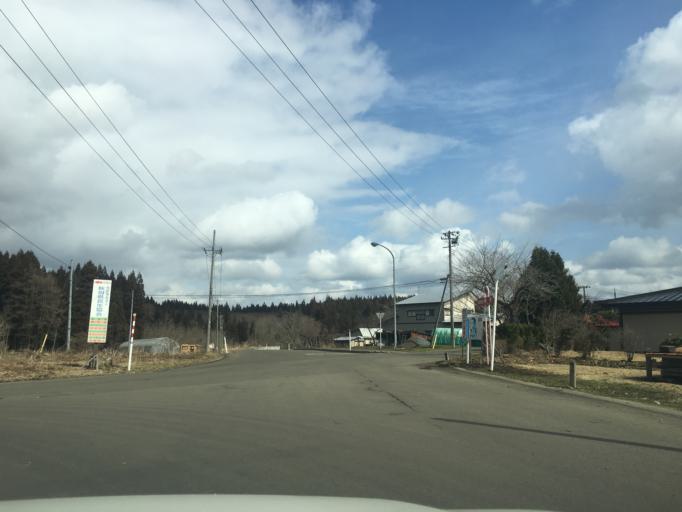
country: JP
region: Akita
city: Takanosu
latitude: 40.1876
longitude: 140.3421
